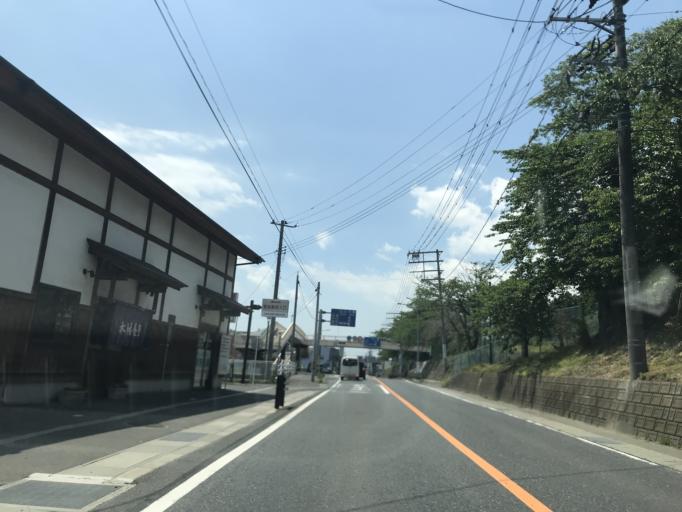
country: JP
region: Miyagi
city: Wakuya
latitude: 38.4795
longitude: 141.0975
